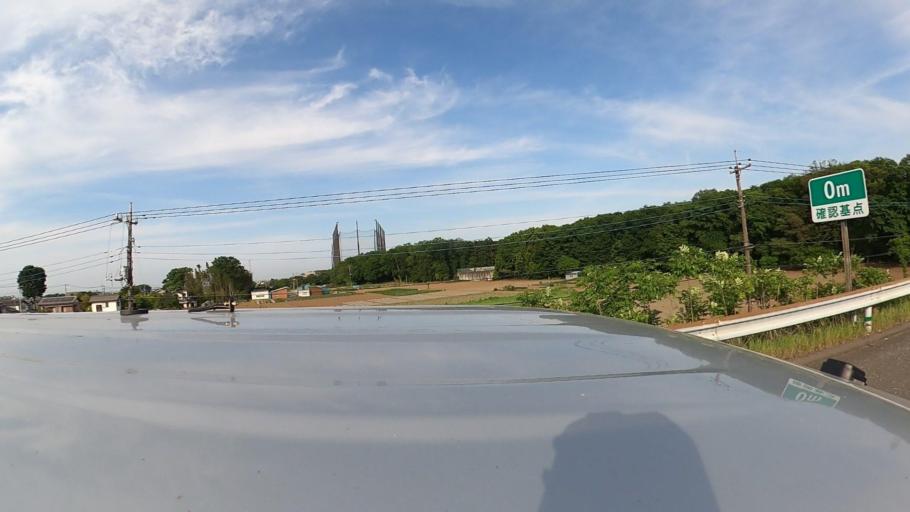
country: JP
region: Saitama
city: Kamifukuoka
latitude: 35.8740
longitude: 139.4813
